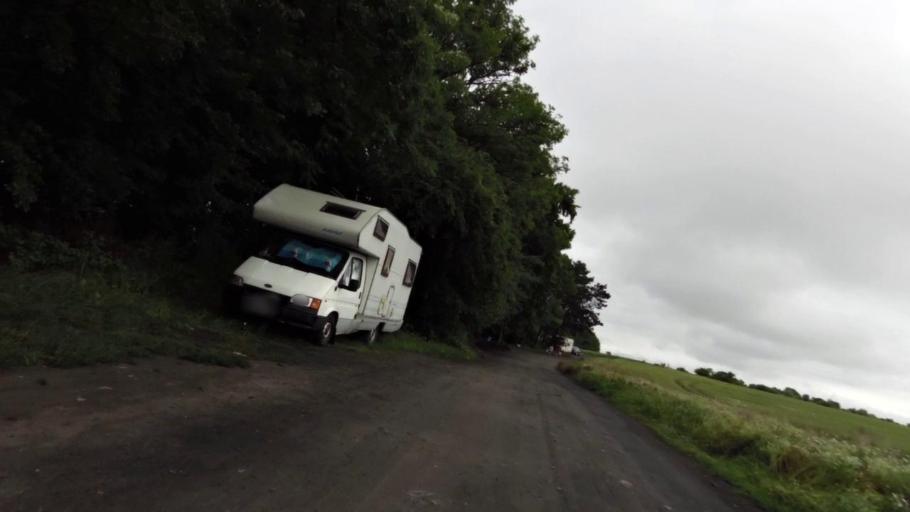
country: PL
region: West Pomeranian Voivodeship
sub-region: Powiat koszalinski
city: Mielno
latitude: 54.2464
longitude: 15.9180
